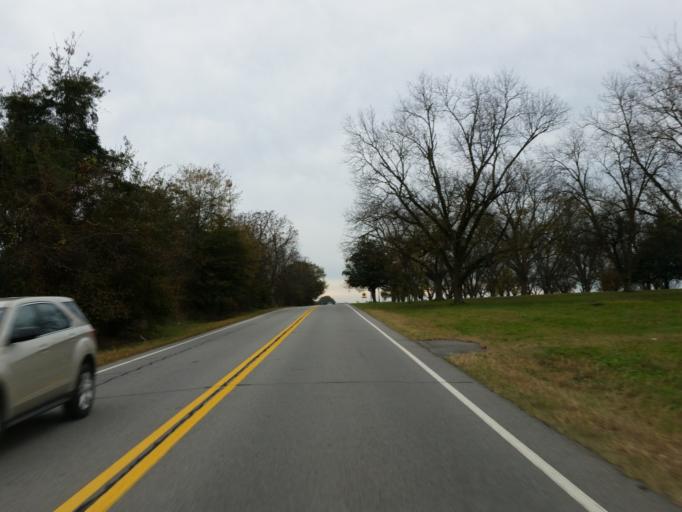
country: US
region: Georgia
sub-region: Dooly County
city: Vienna
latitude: 32.1759
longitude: -83.7655
